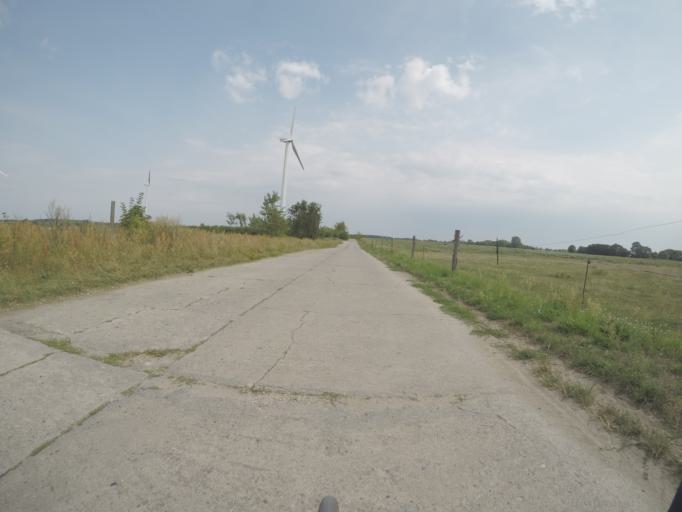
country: DE
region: Berlin
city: Blankenfelde
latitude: 52.6635
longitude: 13.4262
